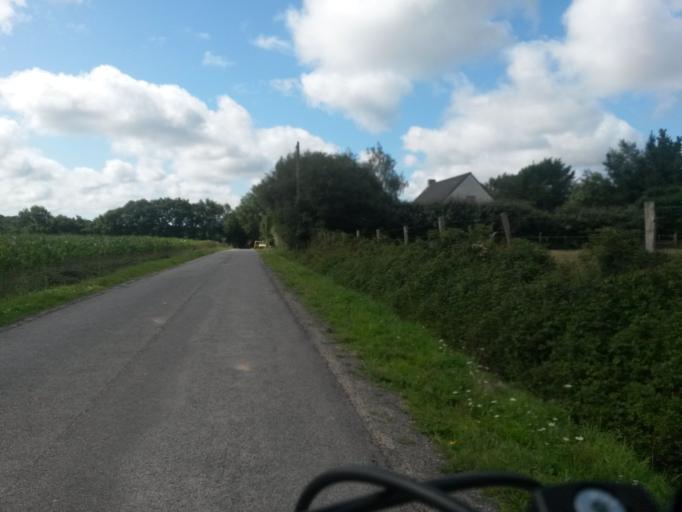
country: FR
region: Pays de la Loire
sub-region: Departement de la Loire-Atlantique
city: Asserac
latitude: 47.3900
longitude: -2.3642
